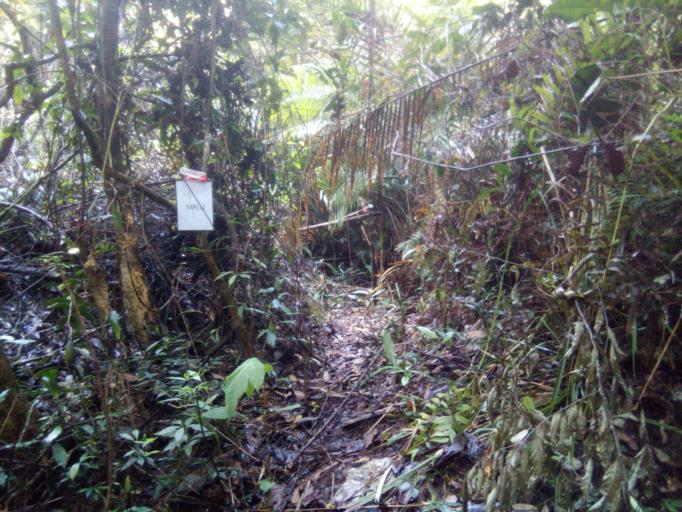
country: MY
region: Penang
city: Tanjung Tokong
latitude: 5.4171
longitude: 100.2605
